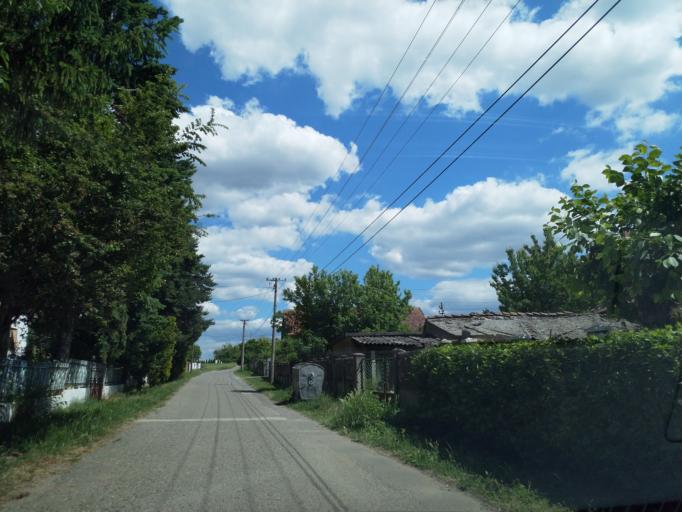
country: RS
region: Central Serbia
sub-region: Pomoravski Okrug
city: Cuprija
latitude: 43.9396
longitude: 21.3105
